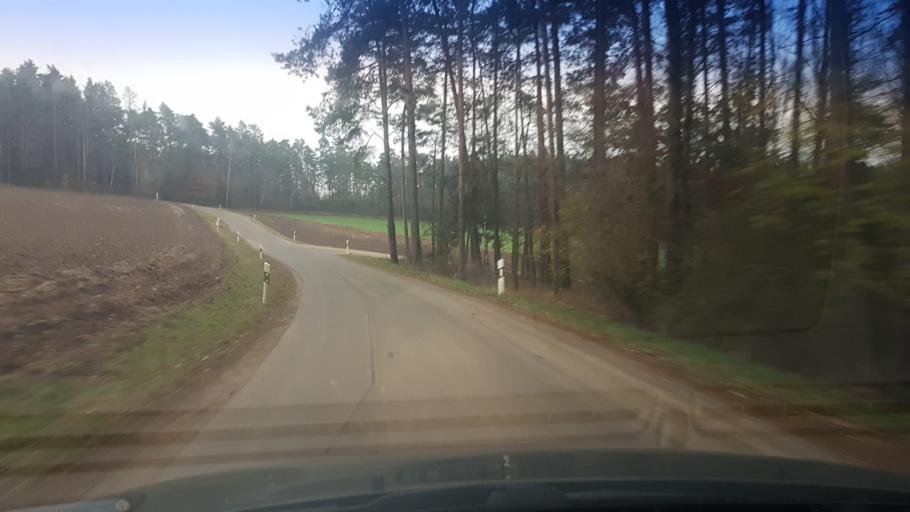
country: DE
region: Bavaria
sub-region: Upper Franconia
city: Weismain
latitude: 50.0439
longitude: 11.2868
